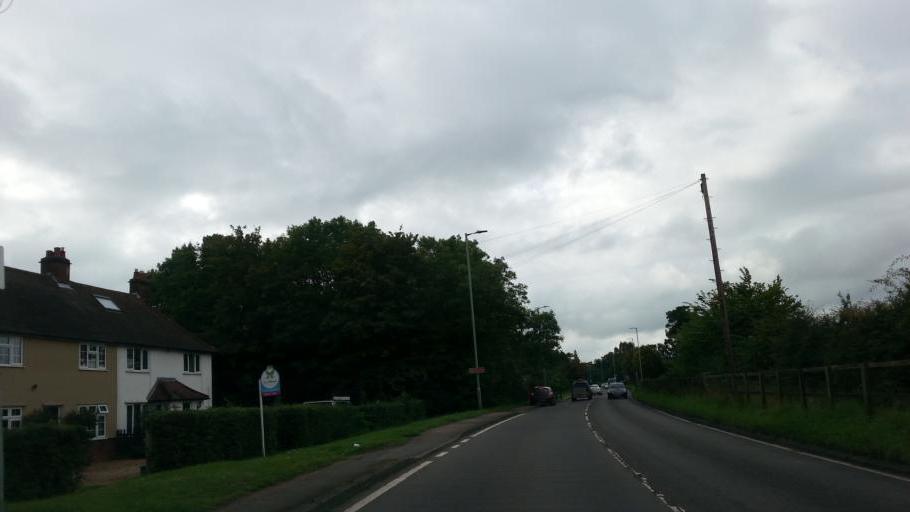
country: GB
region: England
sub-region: Hertfordshire
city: Hitchin
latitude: 51.9712
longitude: -0.2879
